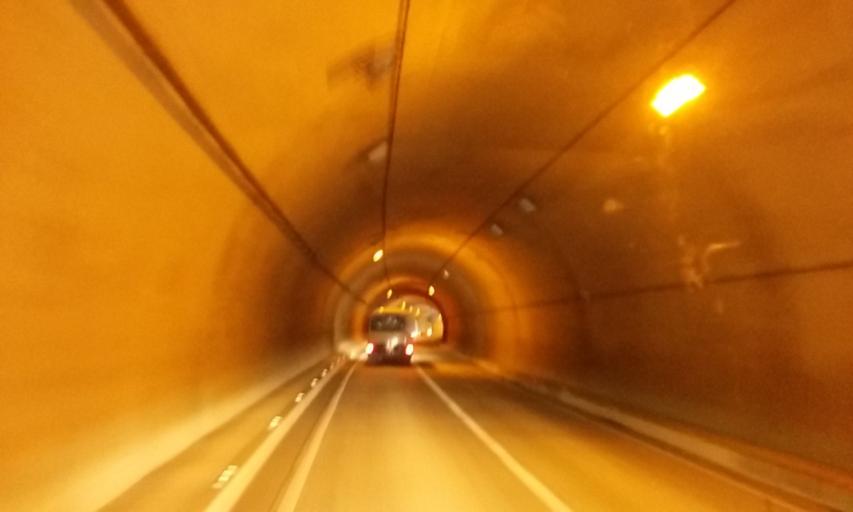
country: JP
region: Ehime
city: Niihama
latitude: 33.8739
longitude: 133.2953
